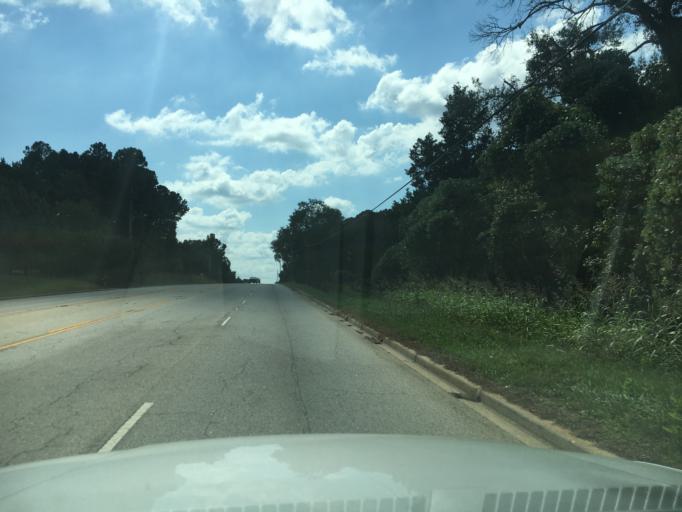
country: US
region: South Carolina
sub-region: Greenwood County
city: Ware Shoals
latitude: 34.3526
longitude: -82.2189
